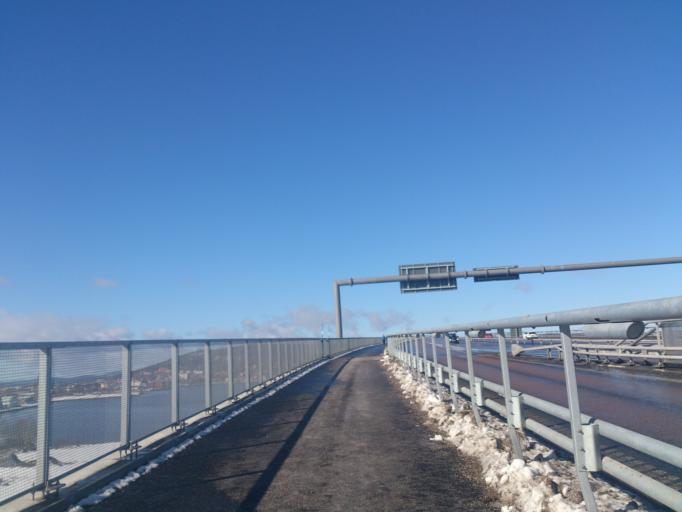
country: SE
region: Vaesternorrland
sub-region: Sundsvalls Kommun
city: Sundsvall
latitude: 62.3830
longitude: 17.3492
